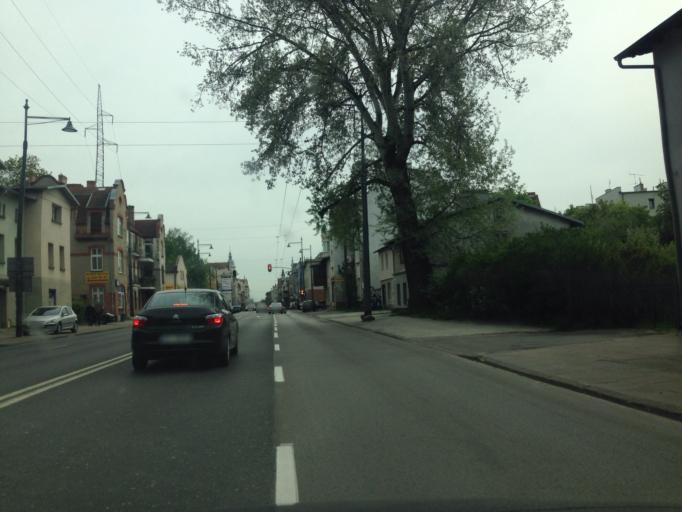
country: PL
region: Pomeranian Voivodeship
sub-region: Sopot
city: Sopot
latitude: 54.4467
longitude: 18.5591
